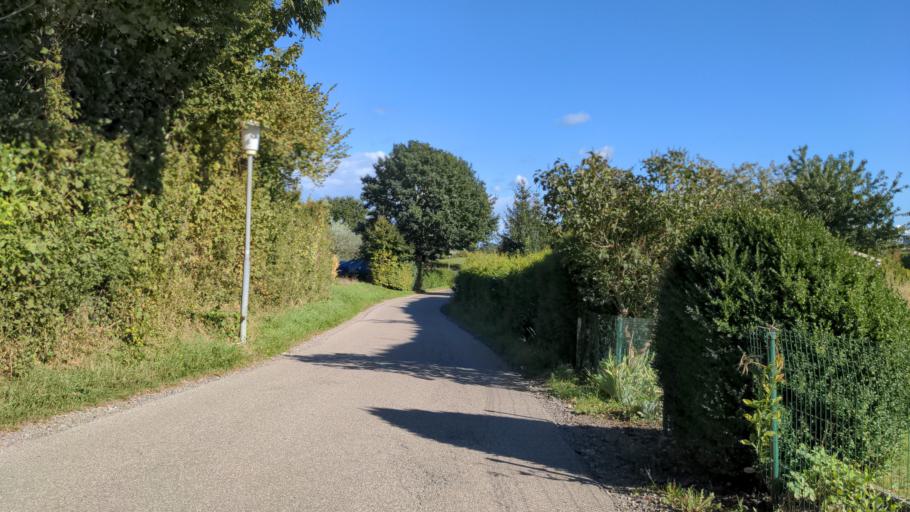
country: DE
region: Schleswig-Holstein
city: Gromitz
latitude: 54.1723
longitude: 10.9443
